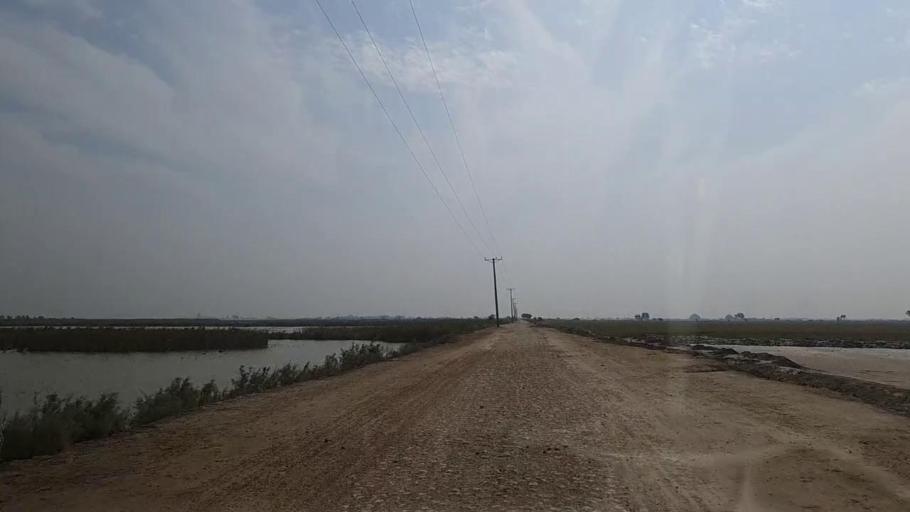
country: PK
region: Sindh
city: Mirpur Batoro
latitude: 24.6067
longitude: 68.2102
